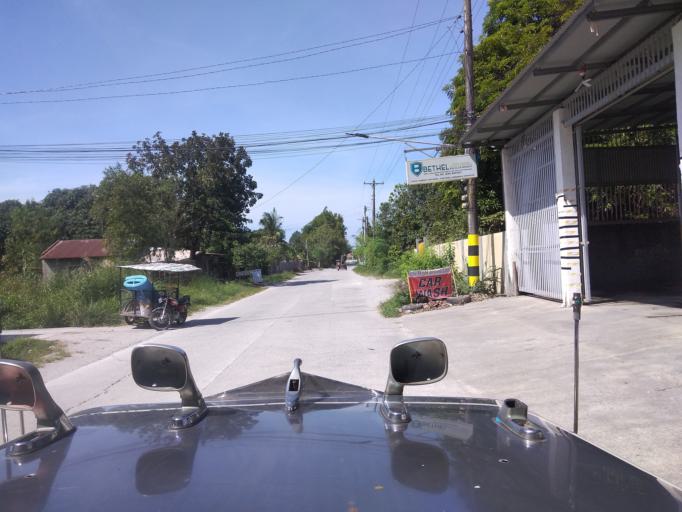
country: PH
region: Central Luzon
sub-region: Province of Pampanga
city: Bacolor
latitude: 15.0161
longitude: 120.6600
